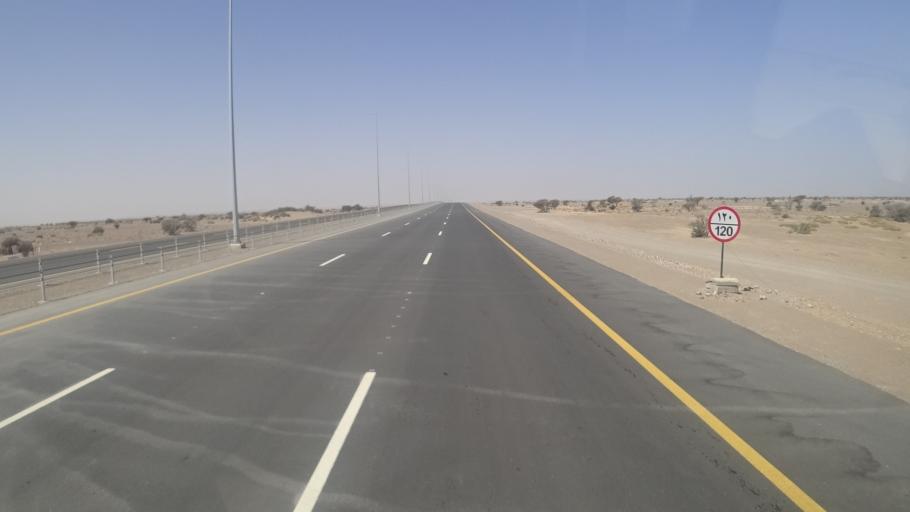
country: OM
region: Ash Sharqiyah
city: Sur
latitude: 22.2754
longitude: 59.2027
